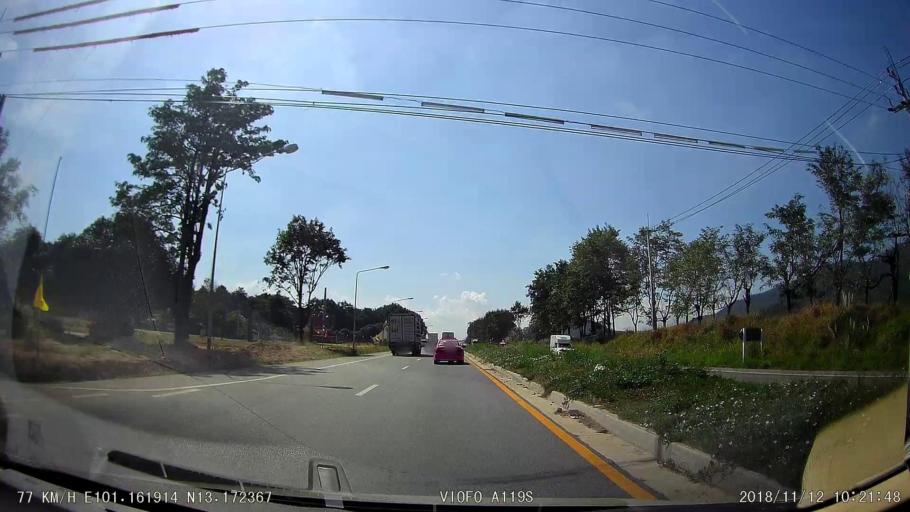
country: TH
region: Chon Buri
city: Ban Bueng
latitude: 13.1720
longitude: 101.1619
